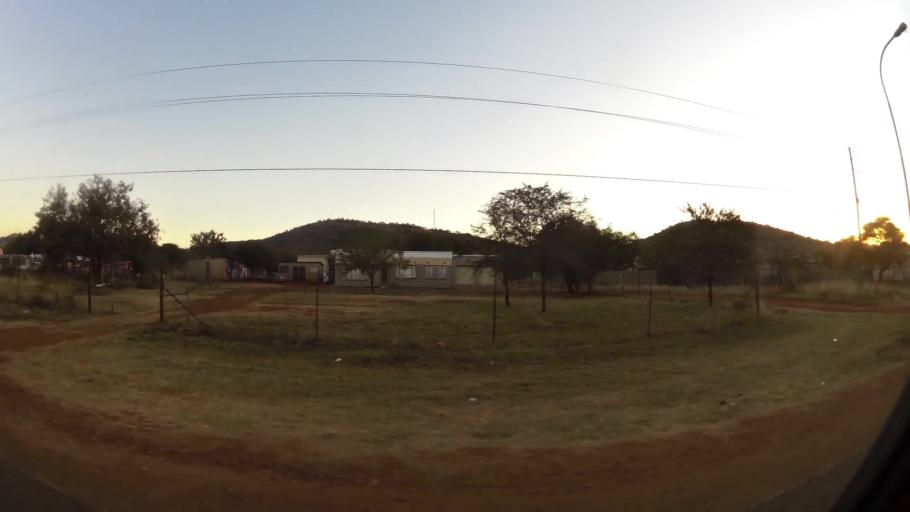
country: ZA
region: North-West
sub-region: Bojanala Platinum District Municipality
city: Rustenburg
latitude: -25.6130
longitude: 27.1911
